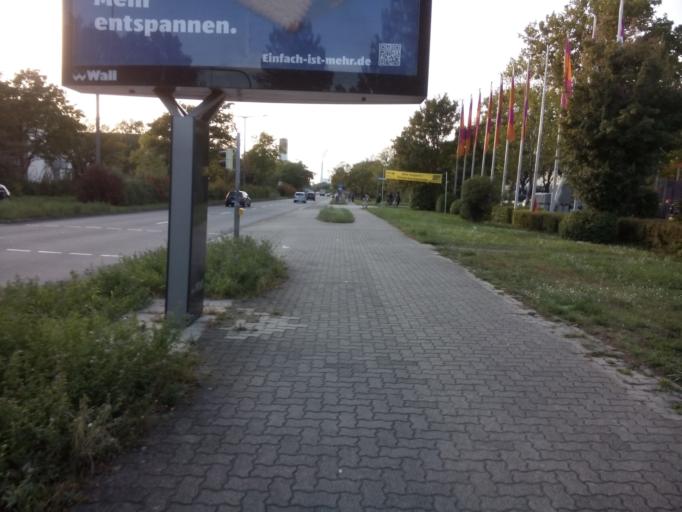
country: DE
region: Baden-Wuerttemberg
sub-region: Karlsruhe Region
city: Karlsruhe
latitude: 48.9979
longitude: 8.3550
